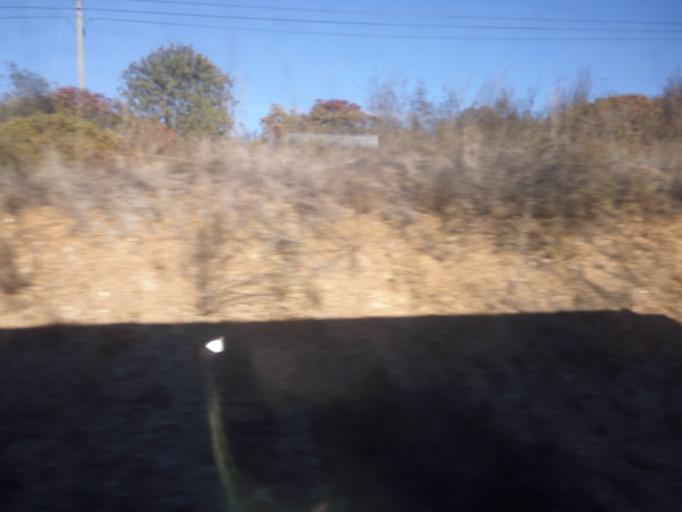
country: PT
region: Faro
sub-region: Silves
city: Sao Bartolomeu de Messines
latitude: 37.3225
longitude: -8.3321
